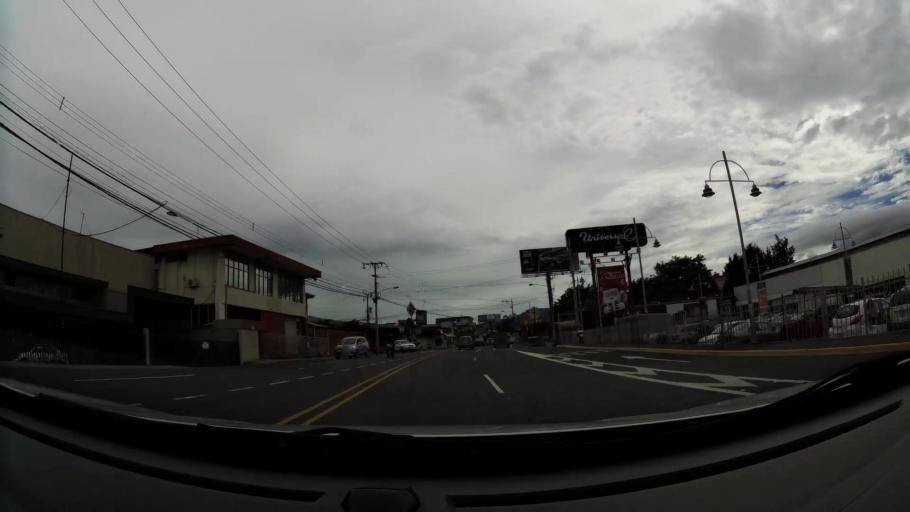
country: CR
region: San Jose
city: San Pedro
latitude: 9.9184
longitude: -84.0462
